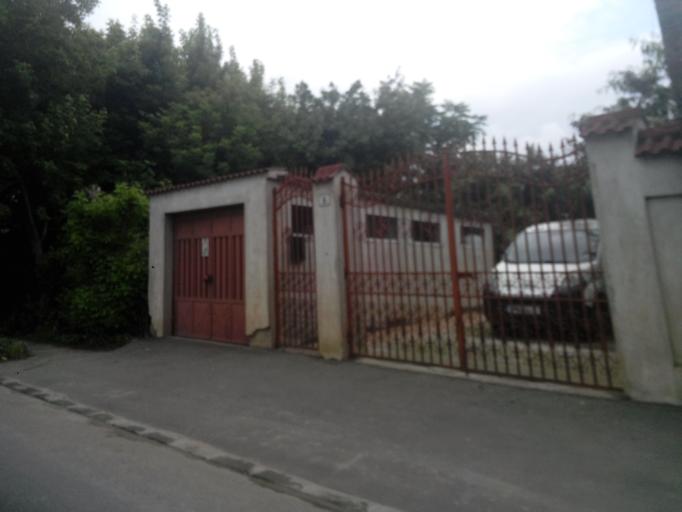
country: RO
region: Ilfov
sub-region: Comuna Chiajna
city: Rosu
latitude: 44.4461
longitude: 26.0310
